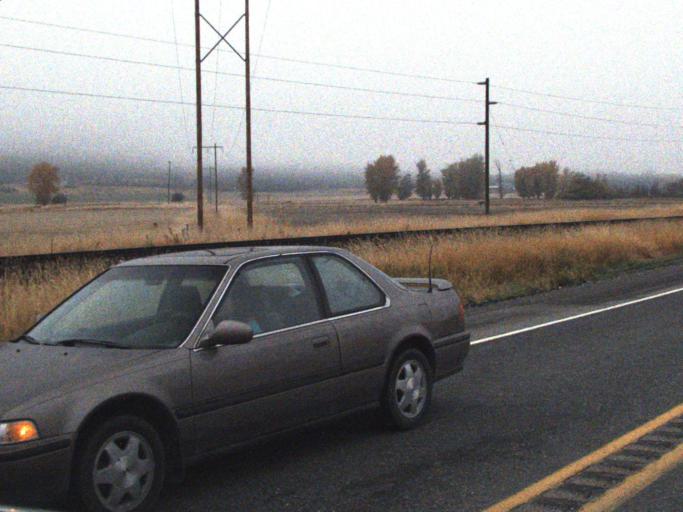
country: US
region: Washington
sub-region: Stevens County
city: Colville
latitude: 48.5689
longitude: -117.9388
